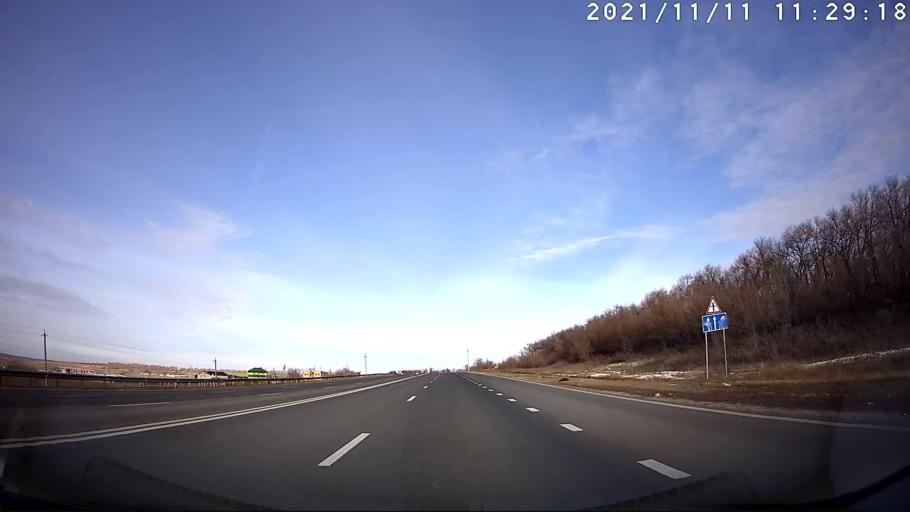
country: RU
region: Samara
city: Varlamovo
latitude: 53.2723
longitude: 48.4794
